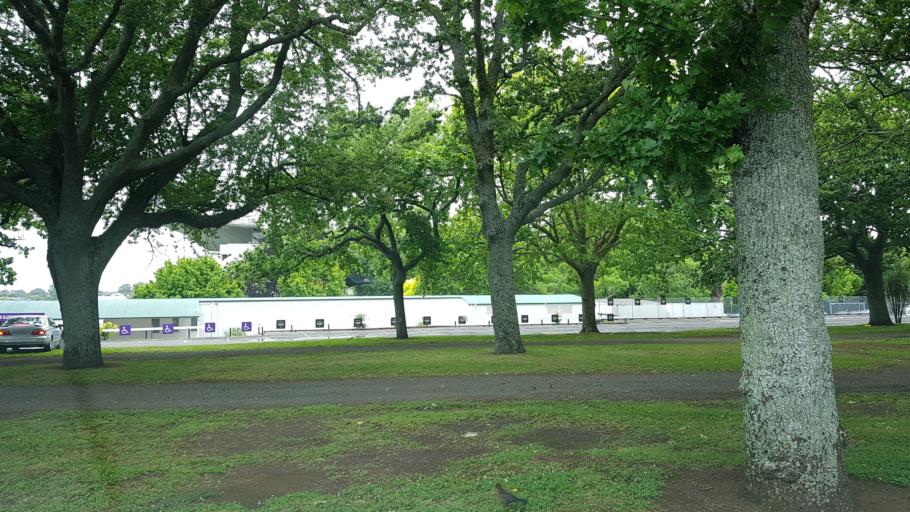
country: NZ
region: Auckland
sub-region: Auckland
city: Auckland
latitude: -36.8893
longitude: 174.8010
